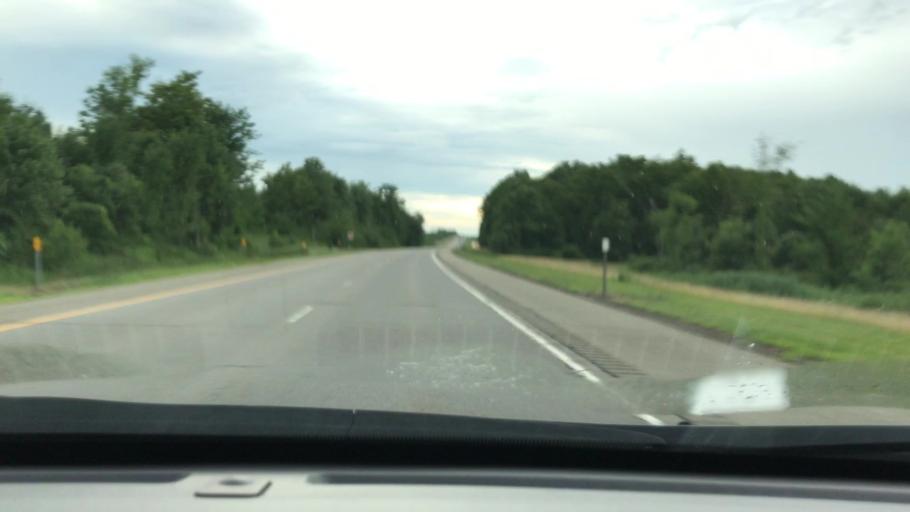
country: US
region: New York
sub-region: Erie County
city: North Boston
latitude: 42.5965
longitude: -78.7439
